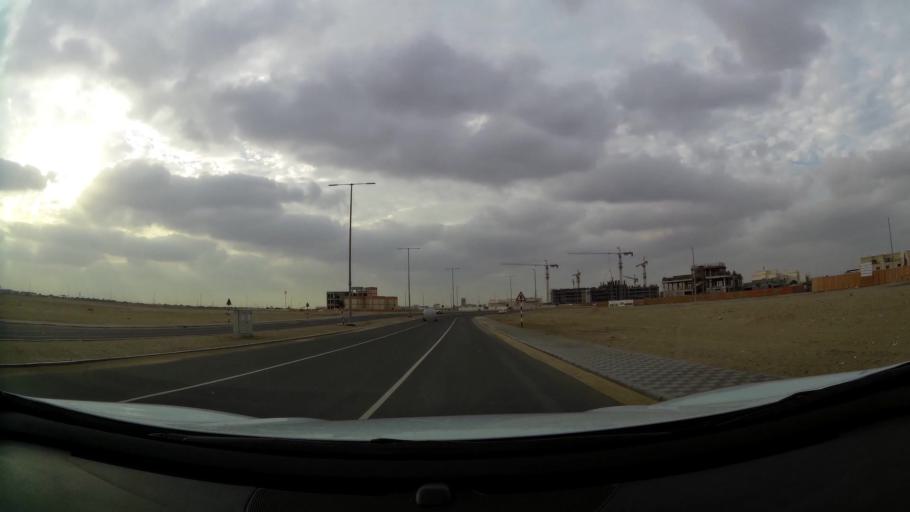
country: AE
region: Abu Dhabi
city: Abu Dhabi
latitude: 24.3505
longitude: 54.5418
